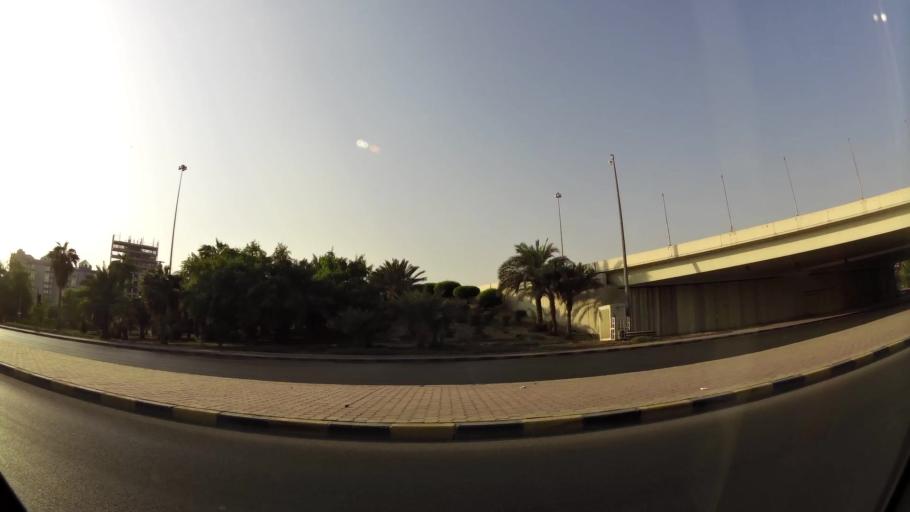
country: KW
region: Muhafazat Hawalli
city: Hawalli
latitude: 29.3436
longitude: 48.0333
